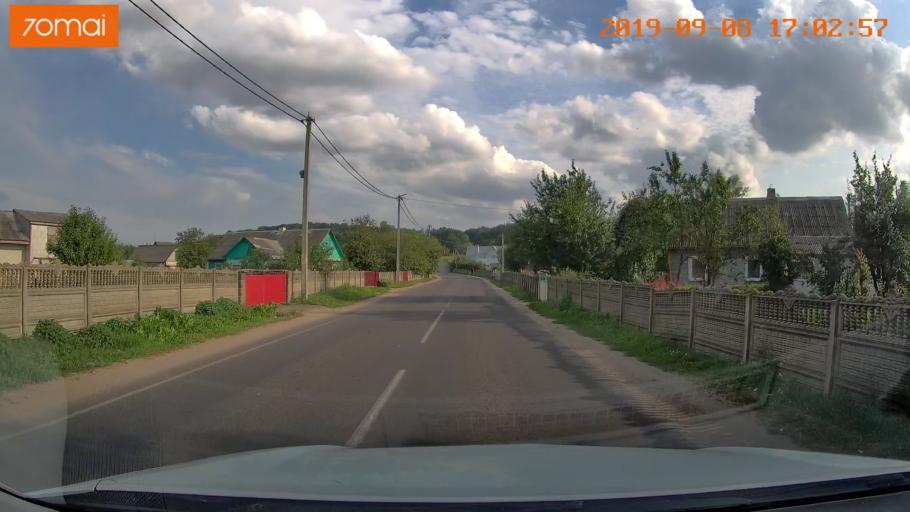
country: BY
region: Grodnenskaya
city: Hrodna
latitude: 53.6988
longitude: 23.9409
